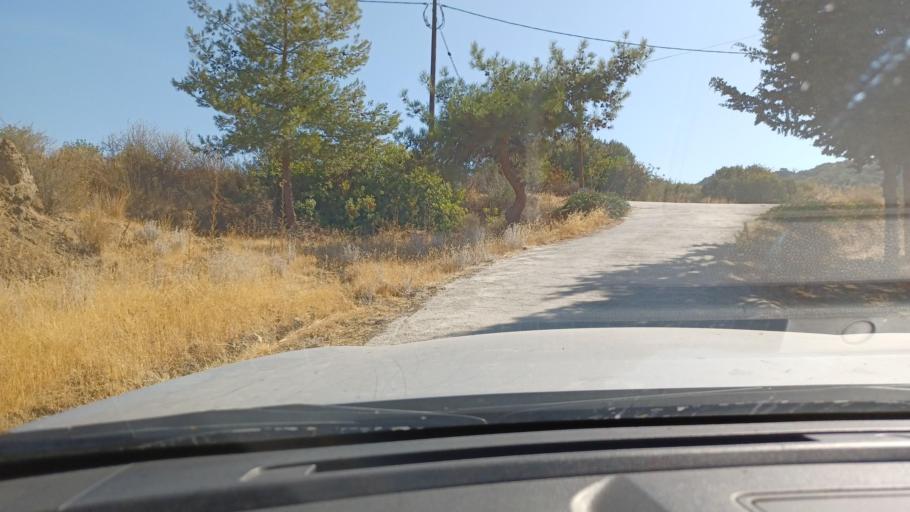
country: CY
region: Pafos
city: Polis
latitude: 35.0008
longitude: 32.4975
